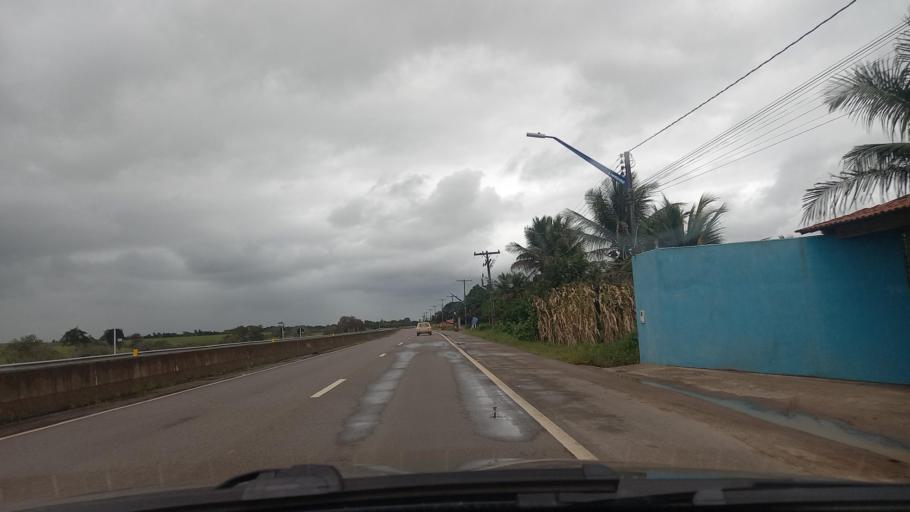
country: BR
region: Alagoas
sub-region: Limoeiro De Anadia
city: Cajueiro
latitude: -9.7482
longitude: -36.4585
